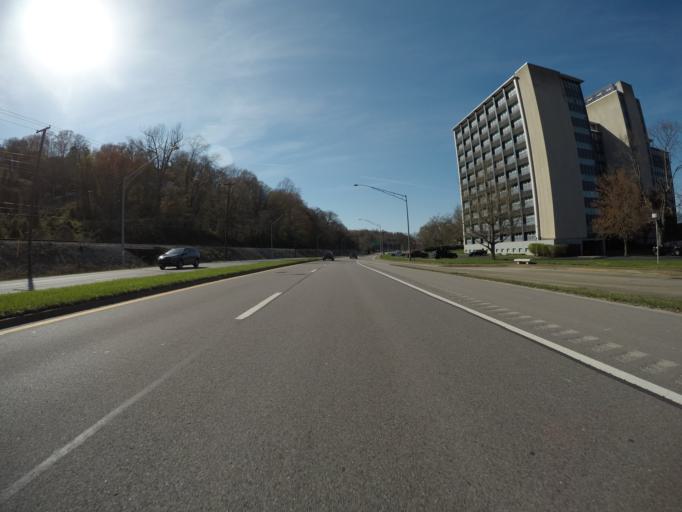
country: US
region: West Virginia
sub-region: Kanawha County
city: Charleston
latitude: 38.3349
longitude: -81.6239
